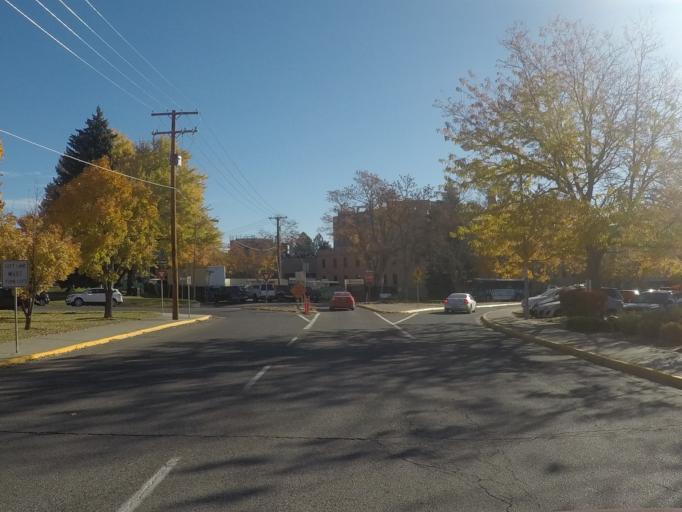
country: US
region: Montana
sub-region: Yellowstone County
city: Billings
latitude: 45.7939
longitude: -108.5217
